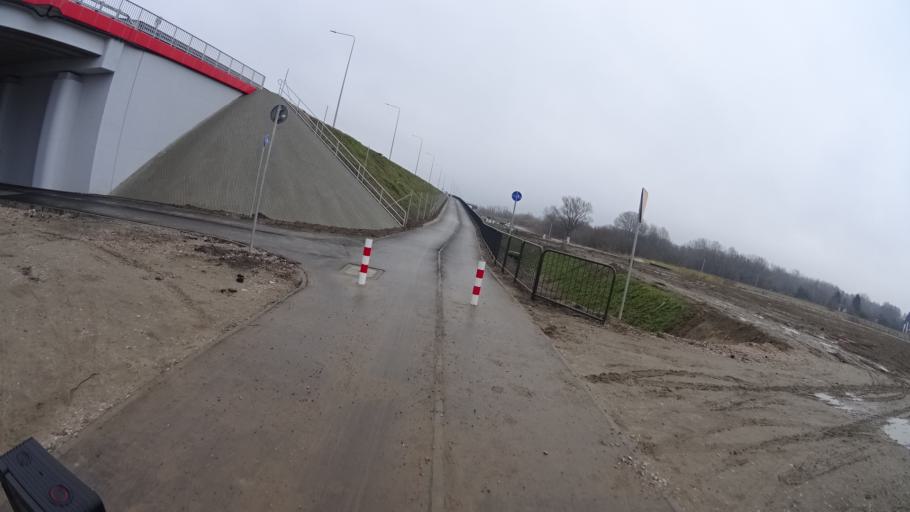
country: PL
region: Masovian Voivodeship
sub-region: Warszawa
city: Wilanow
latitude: 52.1588
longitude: 21.1317
